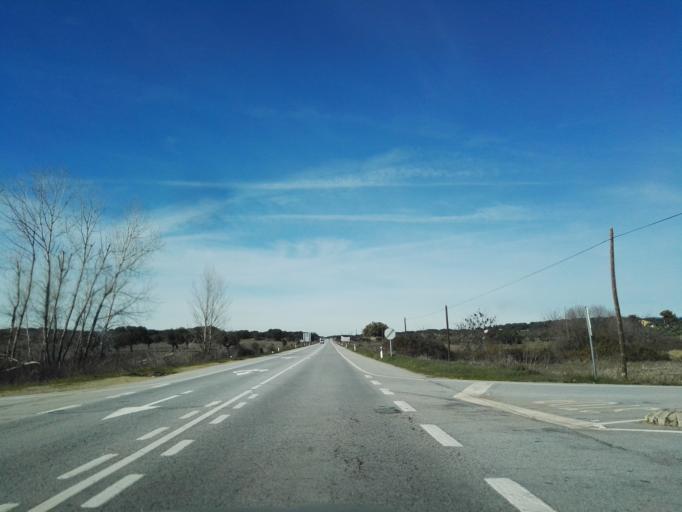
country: PT
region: Portalegre
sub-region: Arronches
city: Arronches
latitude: 39.1603
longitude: -7.3213
